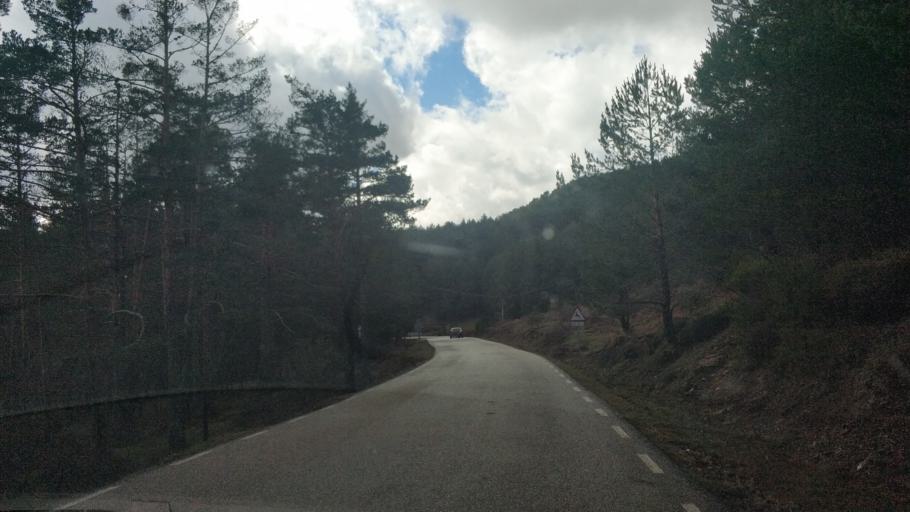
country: ES
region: Castille and Leon
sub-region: Provincia de Burgos
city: Neila
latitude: 42.0254
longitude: -3.0122
